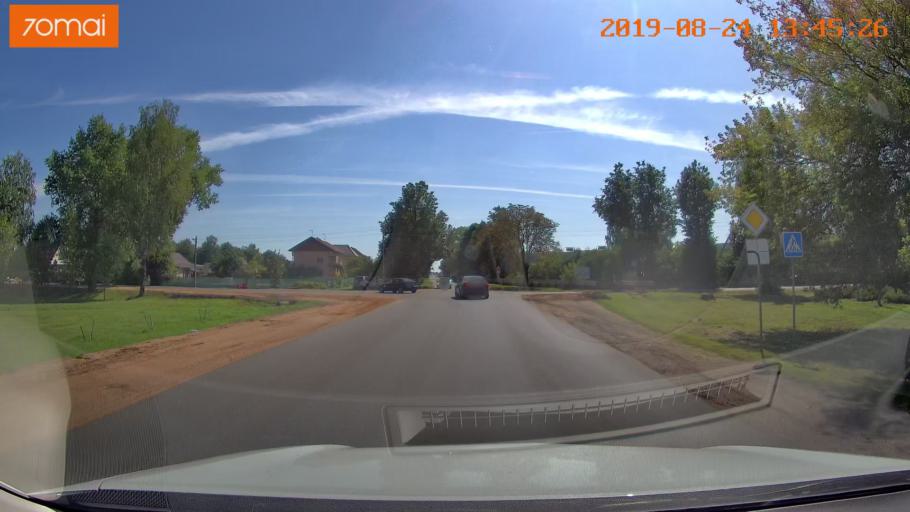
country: BY
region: Minsk
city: Samakhvalavichy
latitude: 53.6802
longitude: 27.5286
